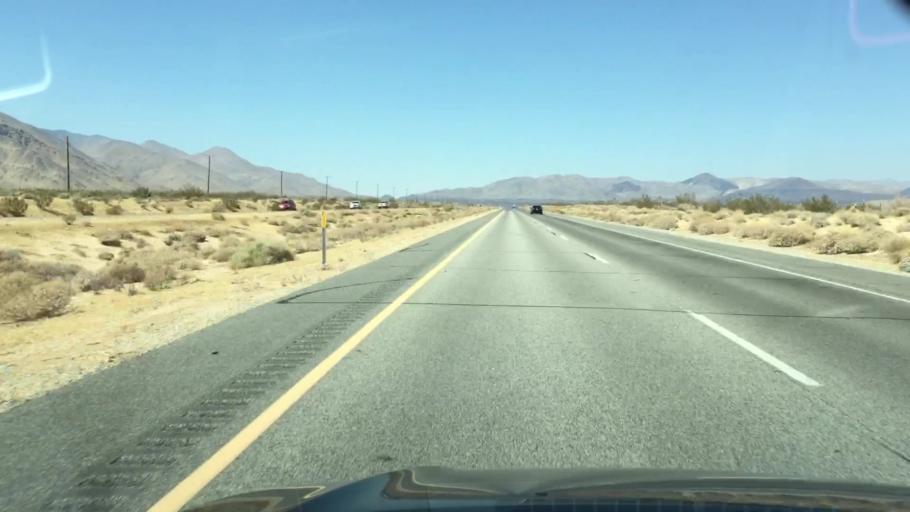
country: US
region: California
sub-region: Kern County
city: Inyokern
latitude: 35.7611
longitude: -117.8707
